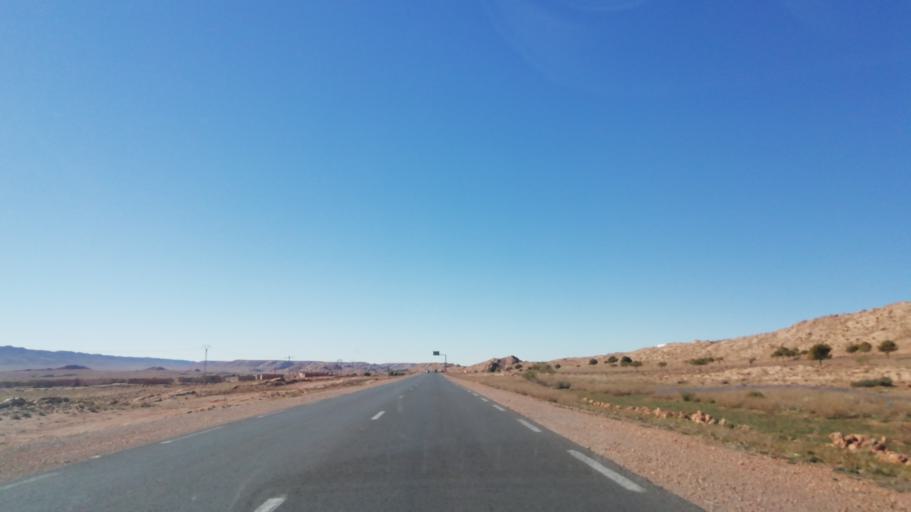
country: DZ
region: El Bayadh
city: El Bayadh
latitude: 33.6141
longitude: 1.1768
